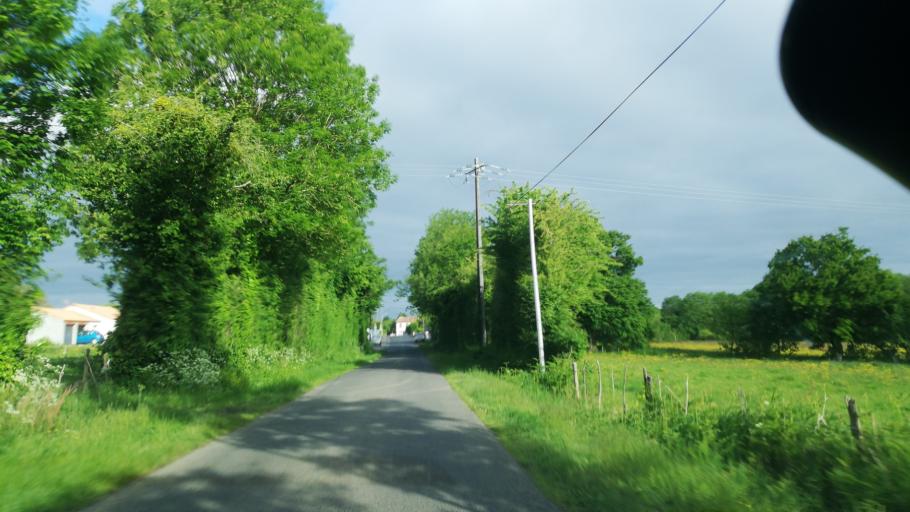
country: FR
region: Poitou-Charentes
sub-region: Departement des Deux-Sevres
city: Moncoutant
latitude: 46.6834
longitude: -0.5714
